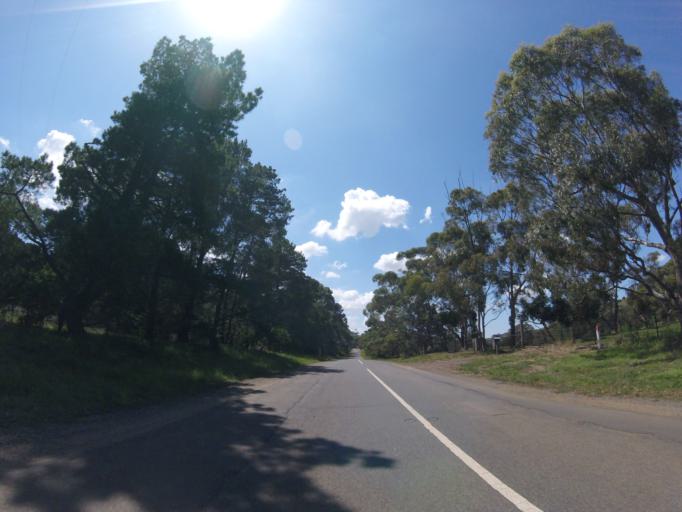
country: AU
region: Victoria
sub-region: Hume
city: Greenvale
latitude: -37.6077
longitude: 144.8049
